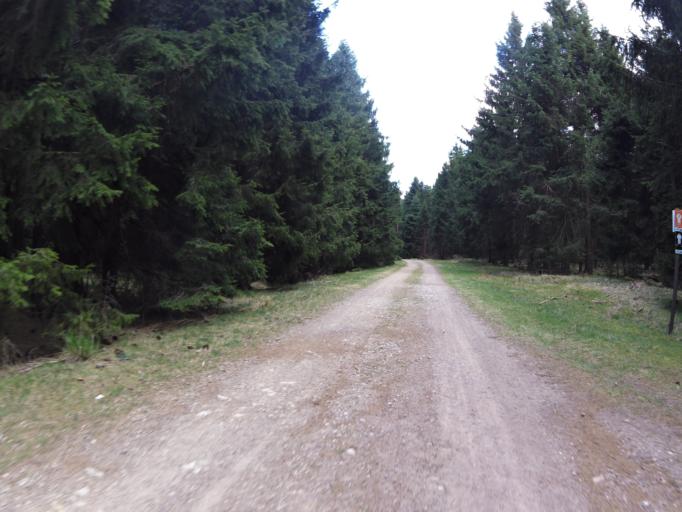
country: DE
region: Thuringia
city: Bermbach
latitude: 50.7292
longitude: 10.6304
